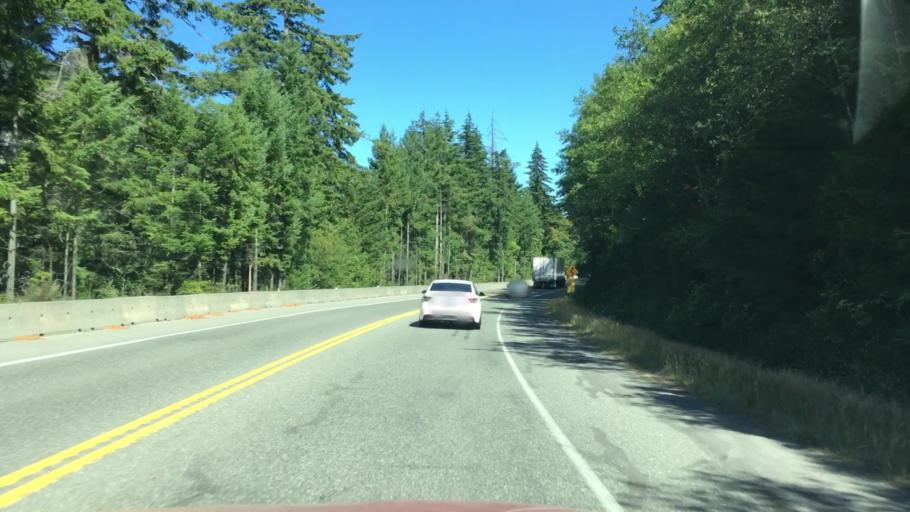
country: CA
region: British Columbia
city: Port Alberni
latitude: 49.2896
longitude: -124.6219
